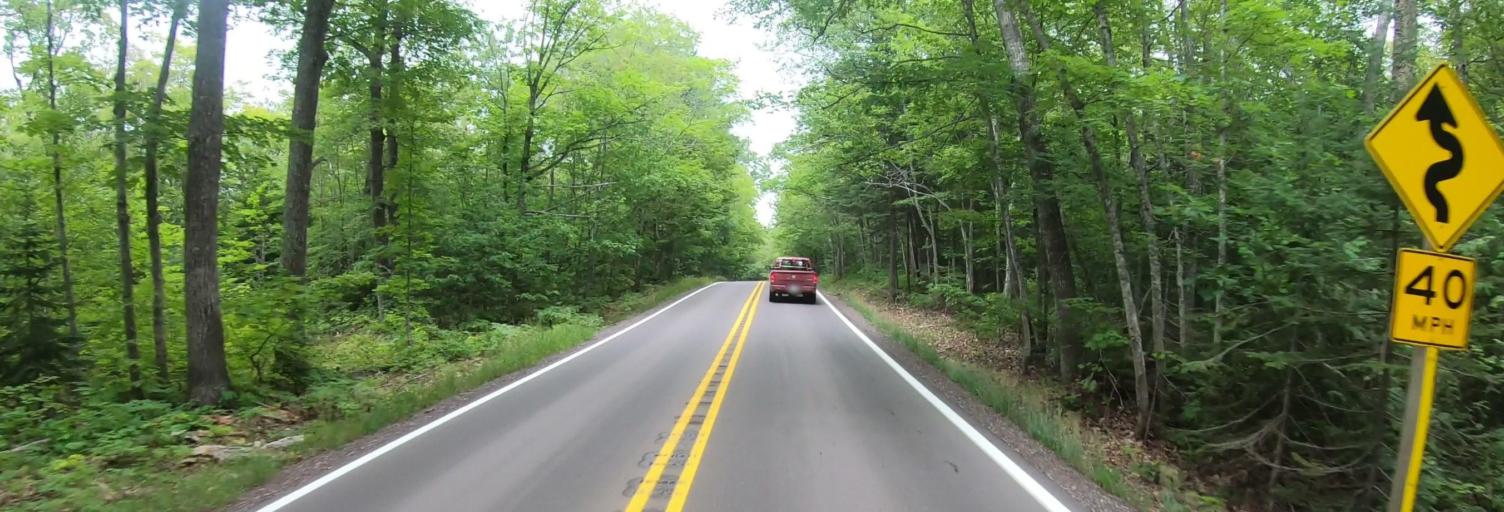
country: US
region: Michigan
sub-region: Keweenaw County
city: Eagle River
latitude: 47.4448
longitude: -87.9300
